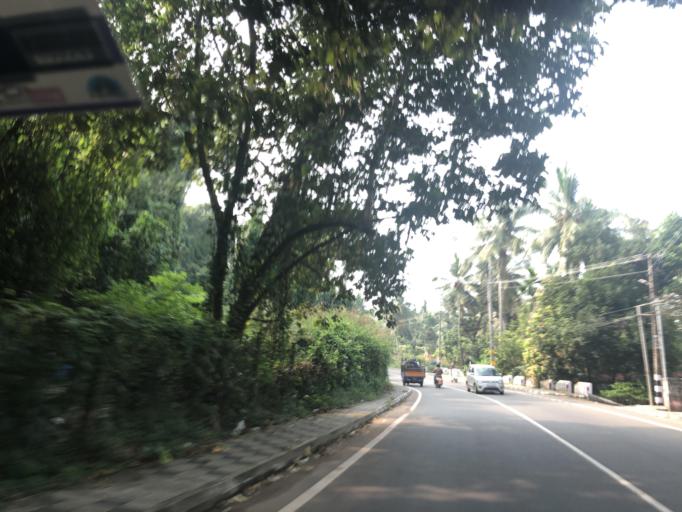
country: IN
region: Kerala
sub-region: Kozhikode
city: Kozhikode
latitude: 11.2915
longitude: 75.7707
